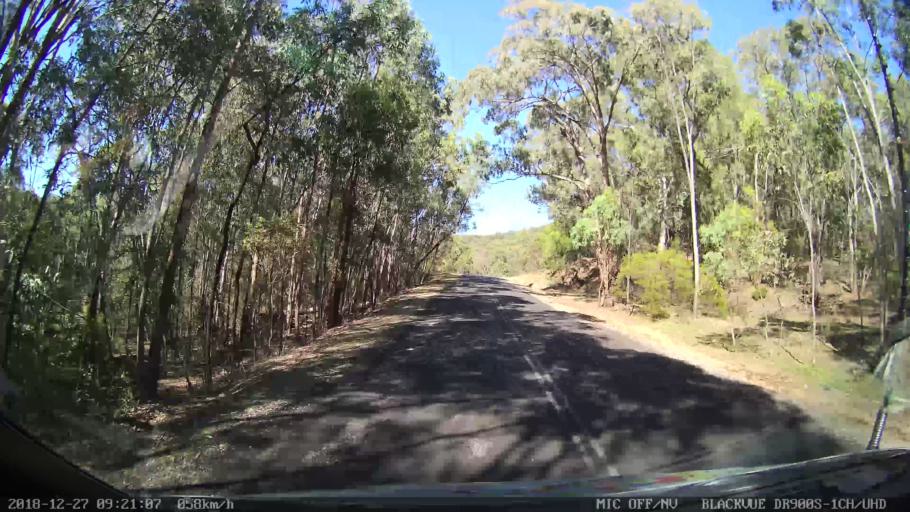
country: AU
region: New South Wales
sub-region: Lithgow
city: Portland
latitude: -33.1220
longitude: 150.0191
